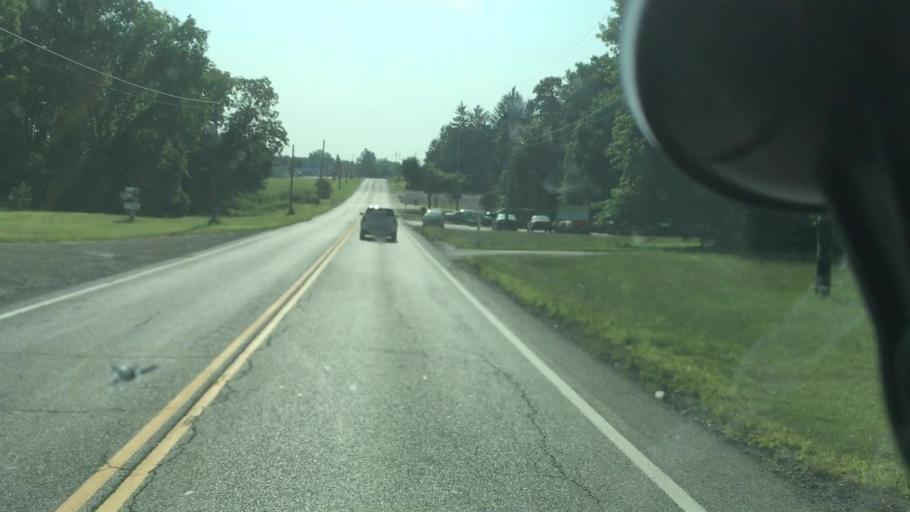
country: US
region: Ohio
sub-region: Mahoning County
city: Lowellville
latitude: 41.0239
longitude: -80.5269
